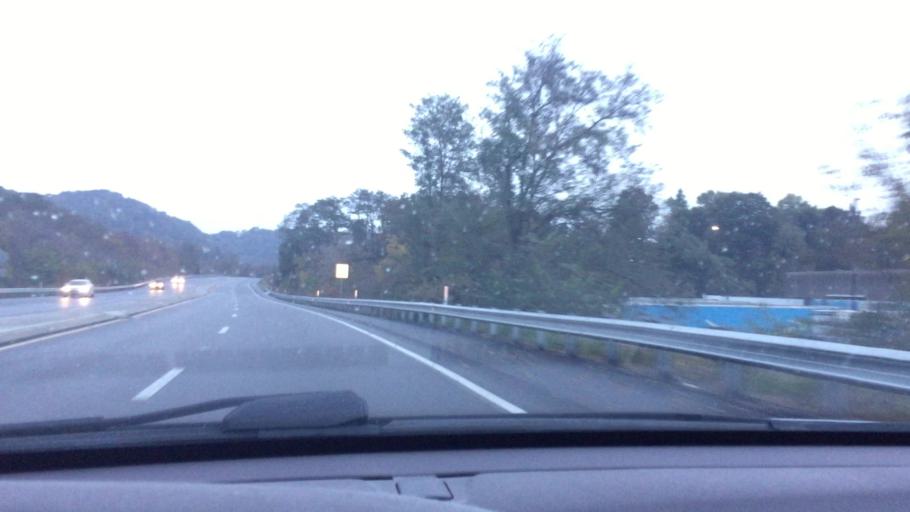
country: US
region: Pennsylvania
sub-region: Allegheny County
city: Ingram
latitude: 40.4433
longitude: -80.0845
